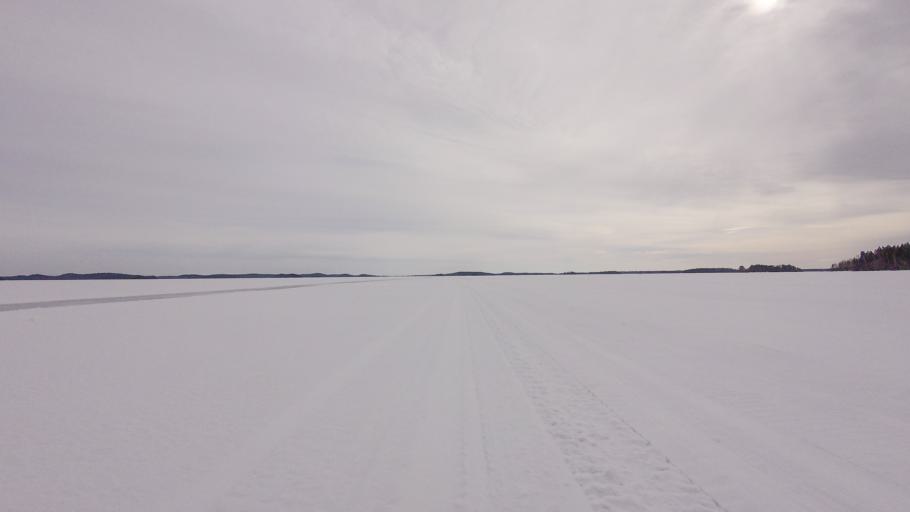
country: FI
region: Southern Savonia
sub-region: Savonlinna
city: Rantasalmi
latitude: 62.1130
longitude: 28.3794
